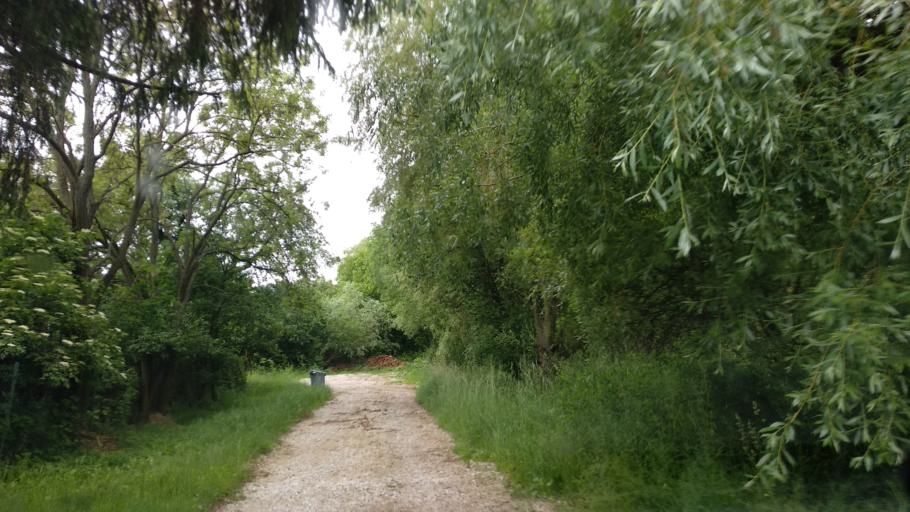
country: SK
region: Nitriansky
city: Trencianske Teplice
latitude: 48.7973
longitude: 18.1248
